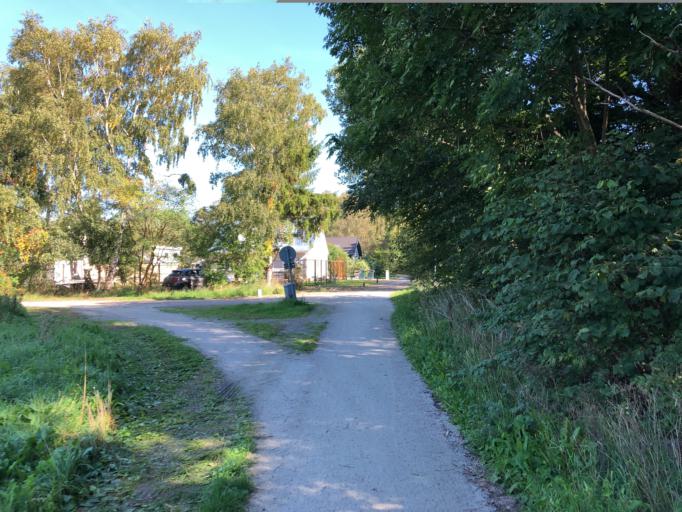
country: SE
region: Skane
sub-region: Lomma Kommun
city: Lomma
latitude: 55.6857
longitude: 13.0708
